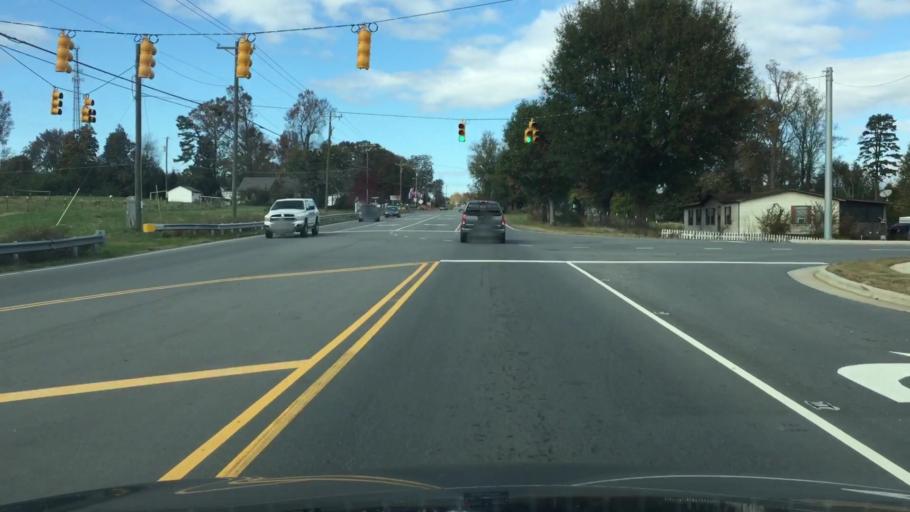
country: US
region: North Carolina
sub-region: Iredell County
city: Troutman
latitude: 35.6637
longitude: -80.8506
